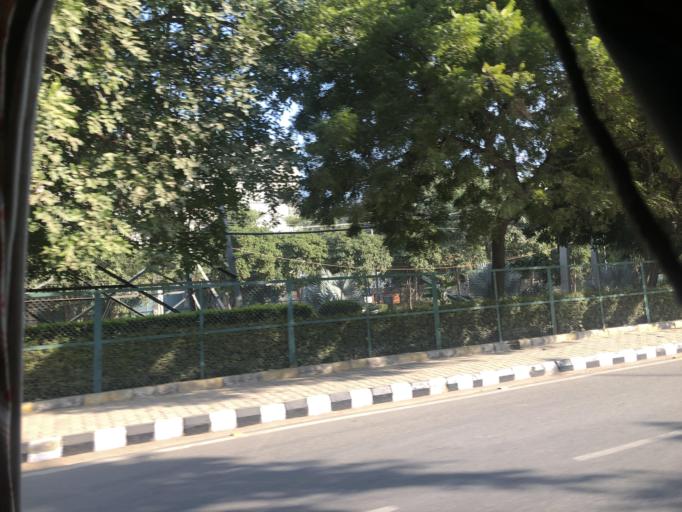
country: IN
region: Haryana
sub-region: Gurgaon
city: Gurgaon
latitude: 28.4563
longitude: 77.0743
